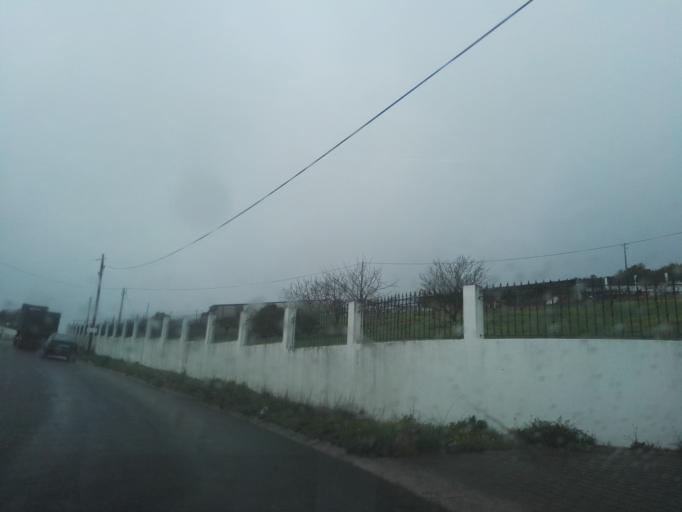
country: PT
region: Lisbon
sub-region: Loures
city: Bucelas
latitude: 38.9173
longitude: -9.0801
